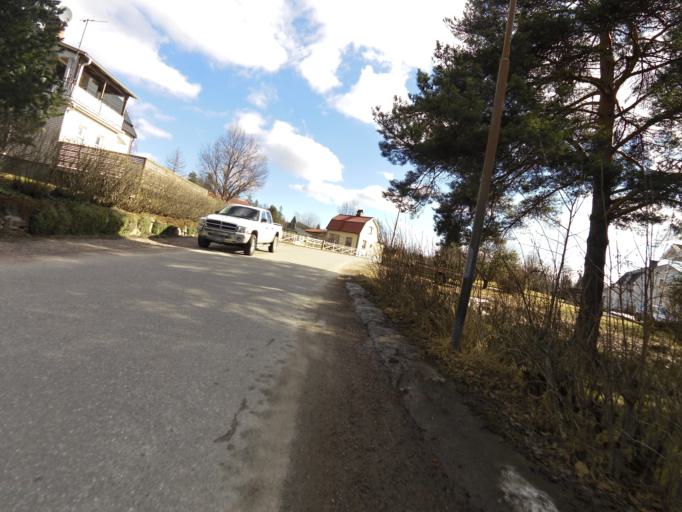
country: SE
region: Gaevleborg
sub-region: Hofors Kommun
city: Hofors
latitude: 60.5386
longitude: 16.2926
